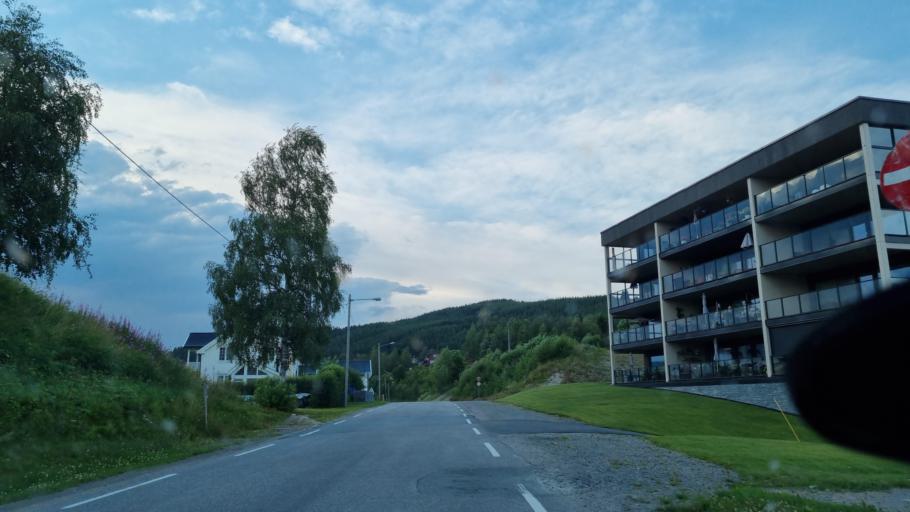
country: NO
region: Hedmark
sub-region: Trysil
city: Innbygda
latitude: 61.3186
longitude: 12.2600
